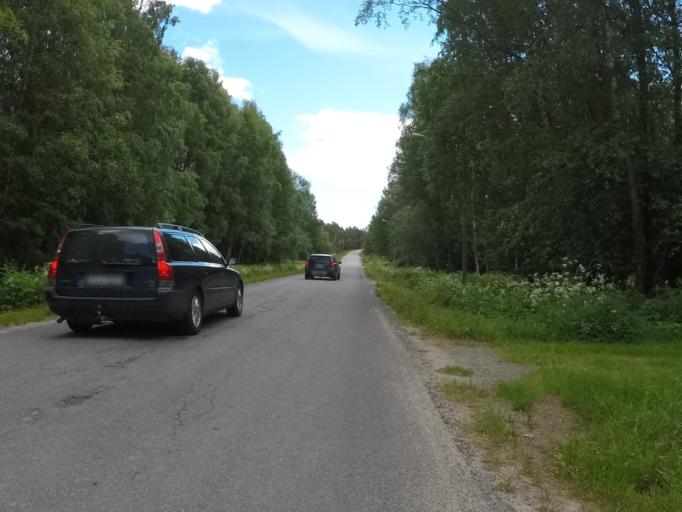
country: SE
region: Vaesterbotten
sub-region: Robertsfors Kommun
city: Robertsfors
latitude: 63.9972
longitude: 20.8132
